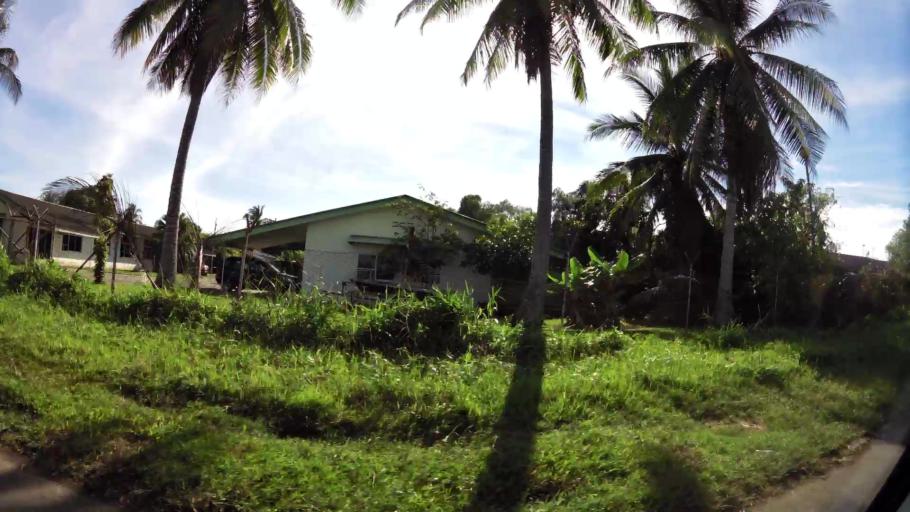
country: BN
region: Belait
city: Kuala Belait
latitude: 4.5767
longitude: 114.2039
